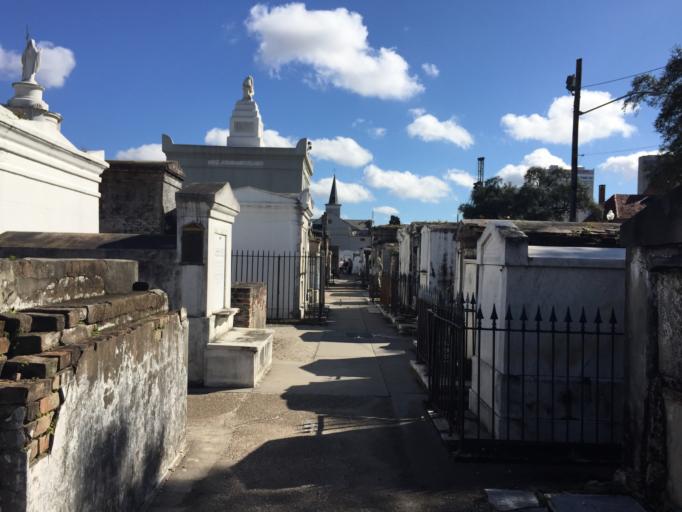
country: US
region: Louisiana
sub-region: Orleans Parish
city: New Orleans
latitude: 29.9593
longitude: -90.0719
